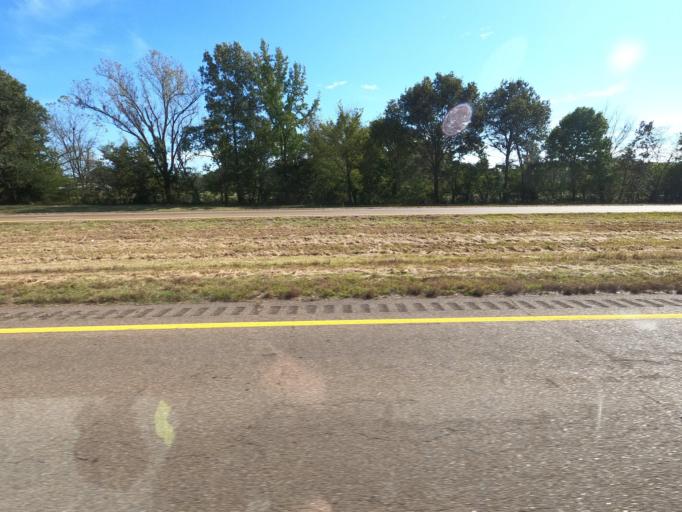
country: US
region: Tennessee
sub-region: Obion County
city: South Fulton
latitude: 36.4881
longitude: -88.9290
